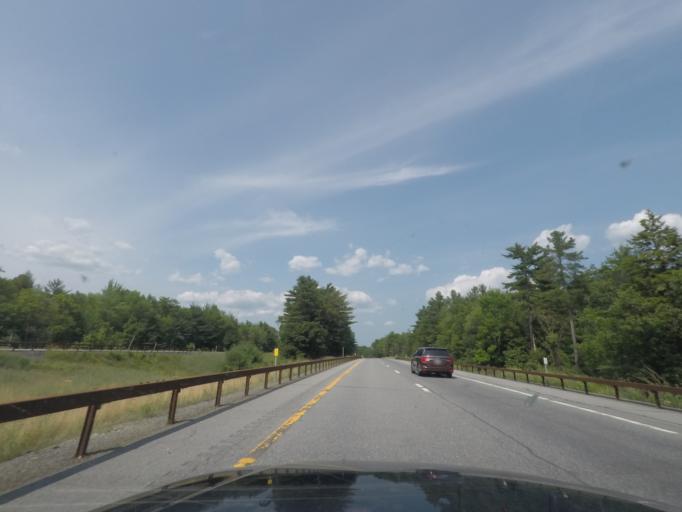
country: US
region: New York
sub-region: Warren County
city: Warrensburg
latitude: 43.8179
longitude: -73.7811
